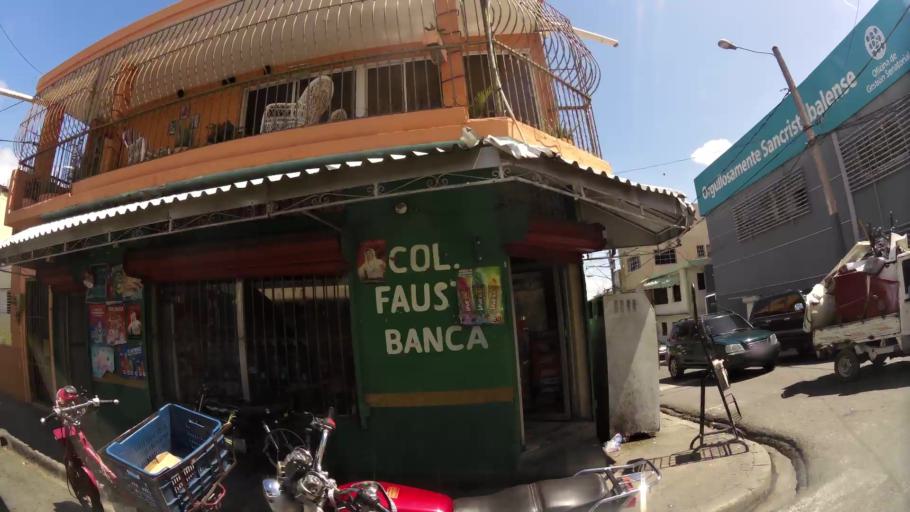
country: DO
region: San Cristobal
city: San Cristobal
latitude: 18.4116
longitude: -70.1083
